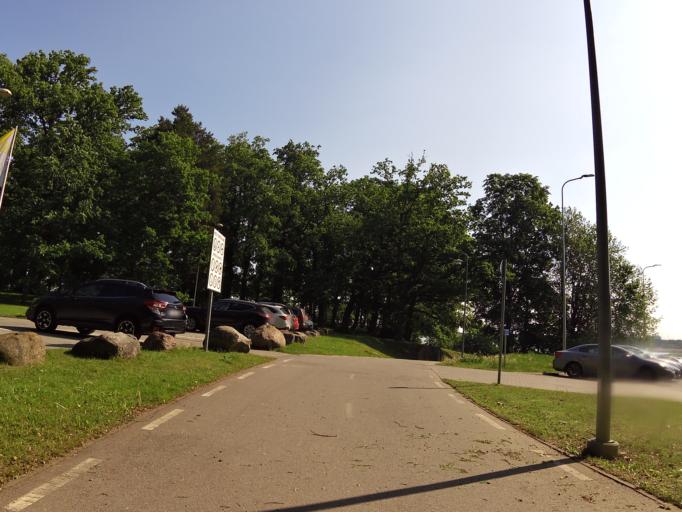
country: EE
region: Harju
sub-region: Saue vald
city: Laagri
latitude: 59.4305
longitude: 24.6505
